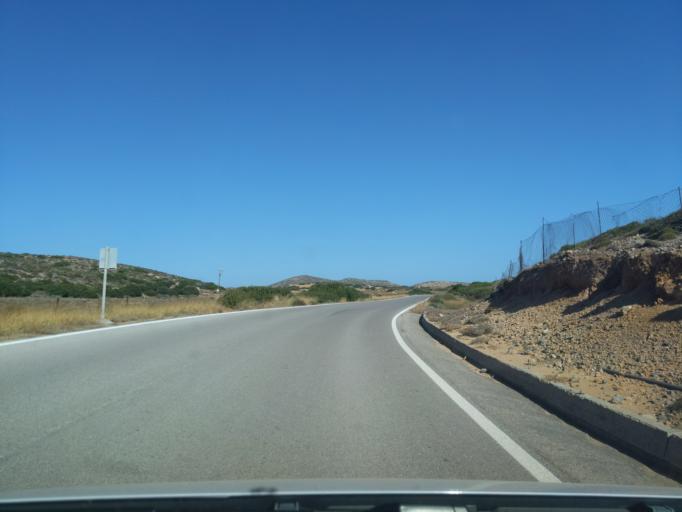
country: GR
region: Crete
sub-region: Nomos Lasithiou
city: Palekastro
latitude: 35.2379
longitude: 26.2489
